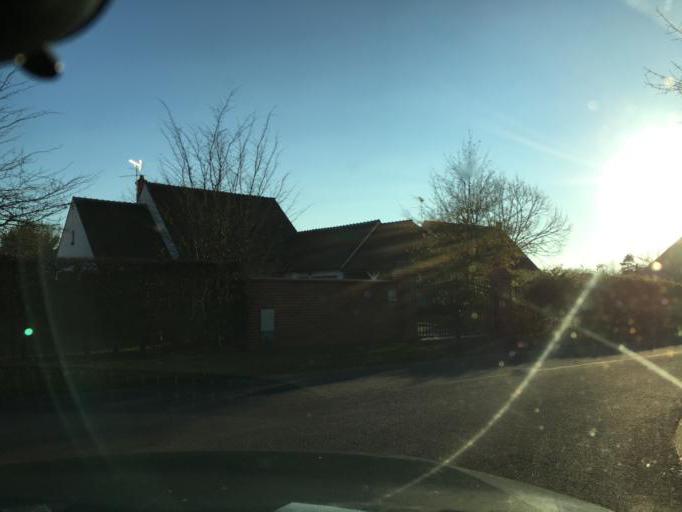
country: FR
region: Centre
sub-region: Departement du Loiret
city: Jouy-le-Potier
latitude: 47.7812
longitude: 1.8751
